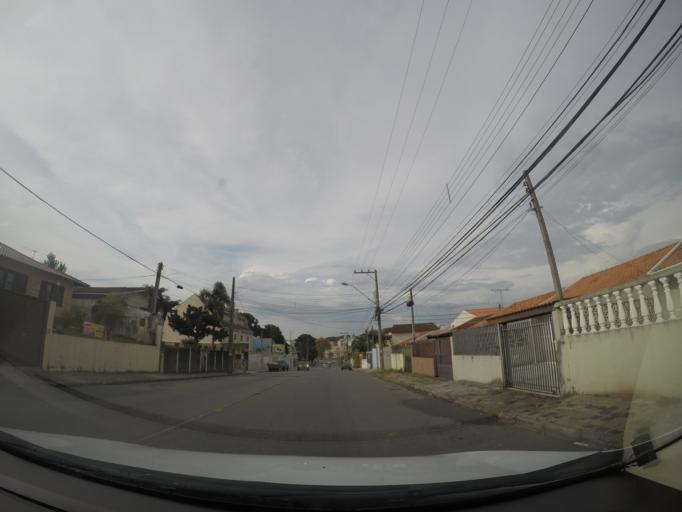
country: BR
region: Parana
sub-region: Sao Jose Dos Pinhais
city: Sao Jose dos Pinhais
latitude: -25.4883
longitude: -49.2251
